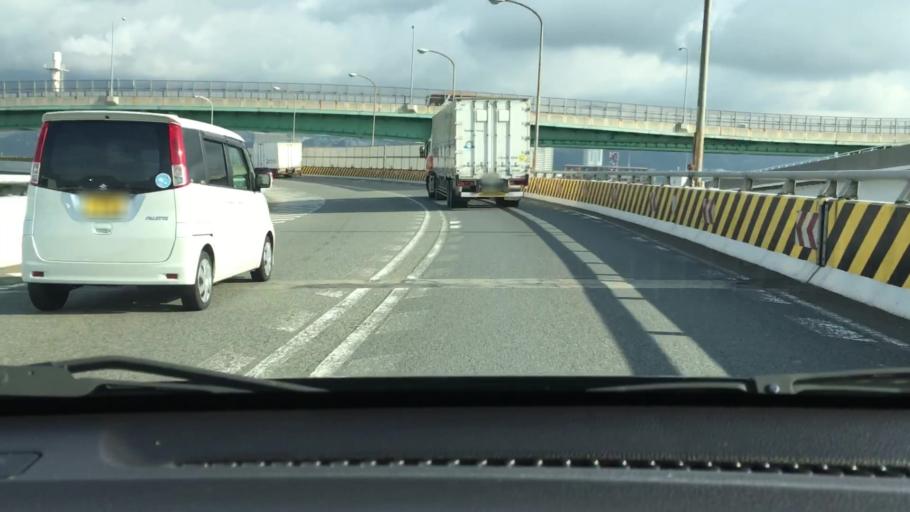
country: JP
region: Hyogo
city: Ashiya
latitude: 34.7046
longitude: 135.2670
